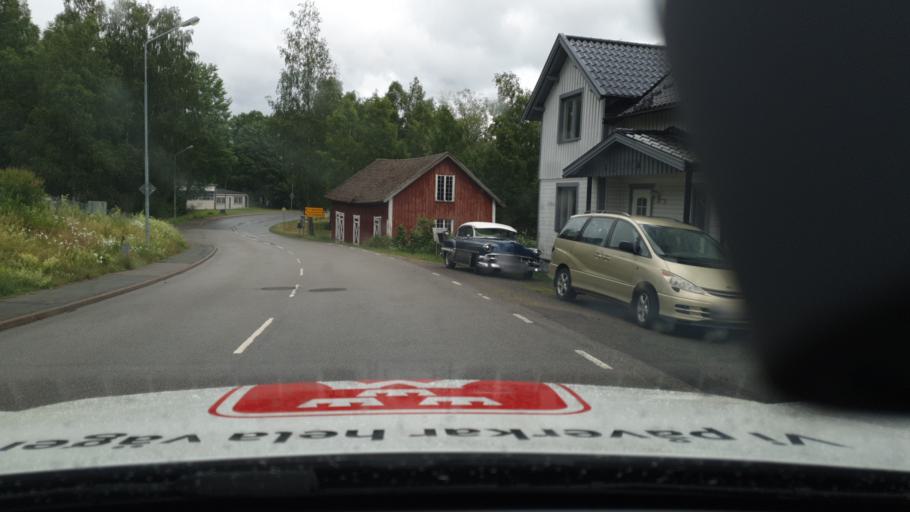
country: SE
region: Joenkoeping
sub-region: Mullsjo Kommun
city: Mullsjoe
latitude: 57.9888
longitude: 13.7621
